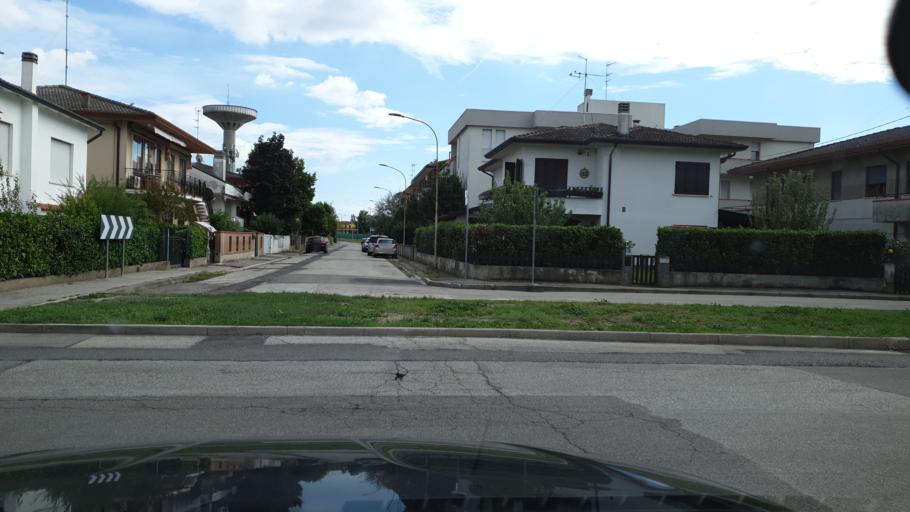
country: IT
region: Veneto
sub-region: Provincia di Rovigo
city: Rovigo
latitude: 45.0711
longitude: 11.7748
